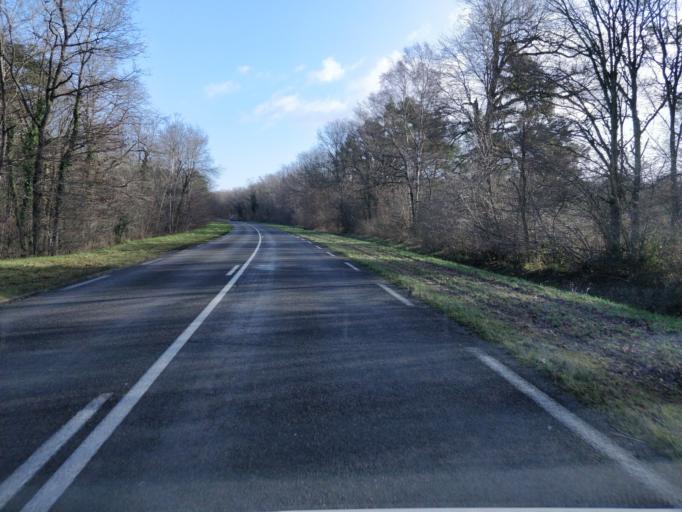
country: FR
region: Ile-de-France
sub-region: Departement de Seine-et-Marne
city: Bagneaux-sur-Loing
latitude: 48.2459
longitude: 2.7788
